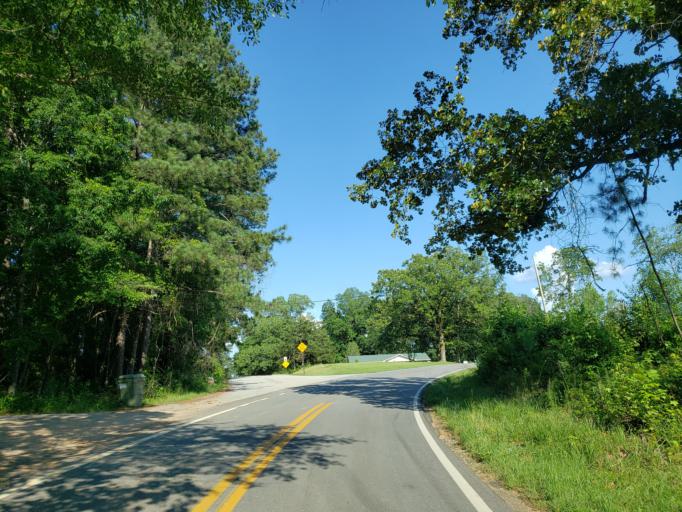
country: US
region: Georgia
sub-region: Haralson County
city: Bremen
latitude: 33.7027
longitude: -85.1032
